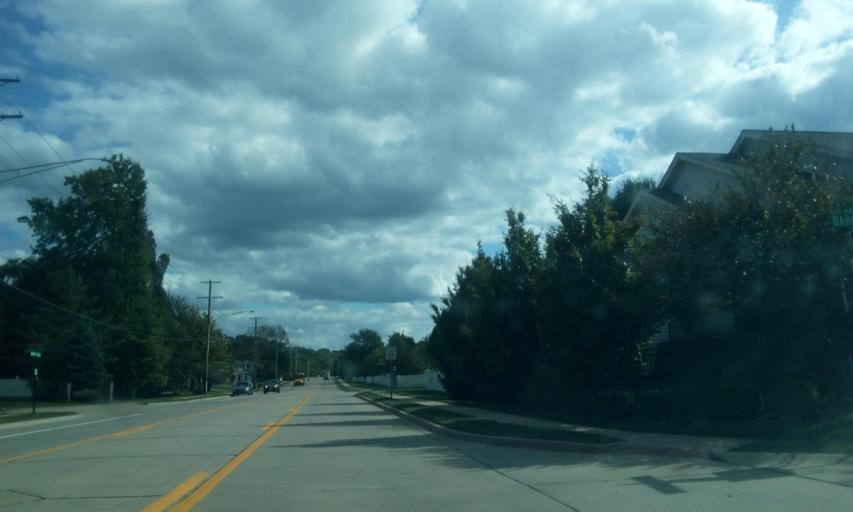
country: US
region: Missouri
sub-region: Saint Louis County
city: Town and Country
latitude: 38.5838
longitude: -90.4665
